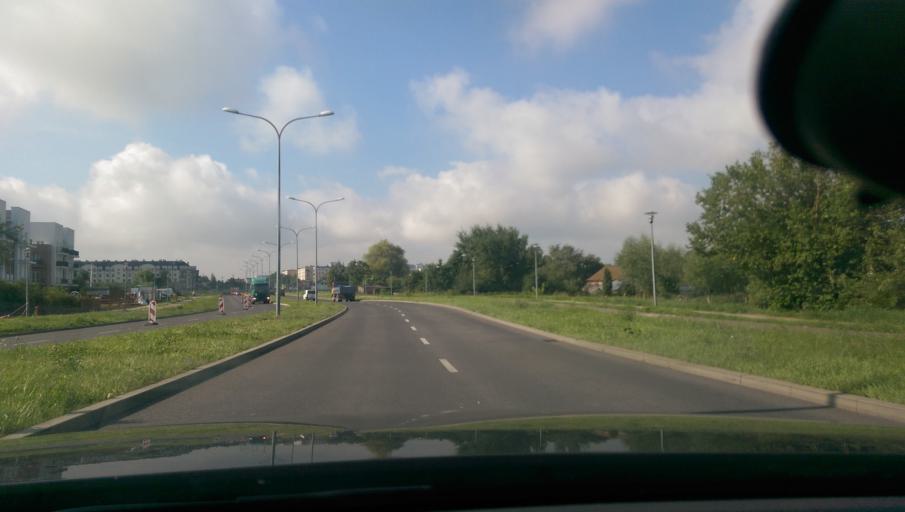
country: PL
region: Masovian Voivodeship
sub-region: Powiat ciechanowski
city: Ciechanow
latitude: 52.8858
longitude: 20.6290
